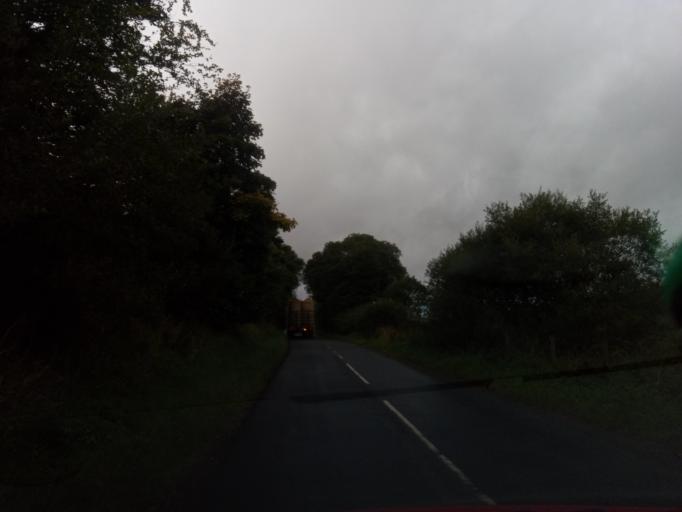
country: GB
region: Scotland
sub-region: The Scottish Borders
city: Duns
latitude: 55.8243
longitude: -2.4231
